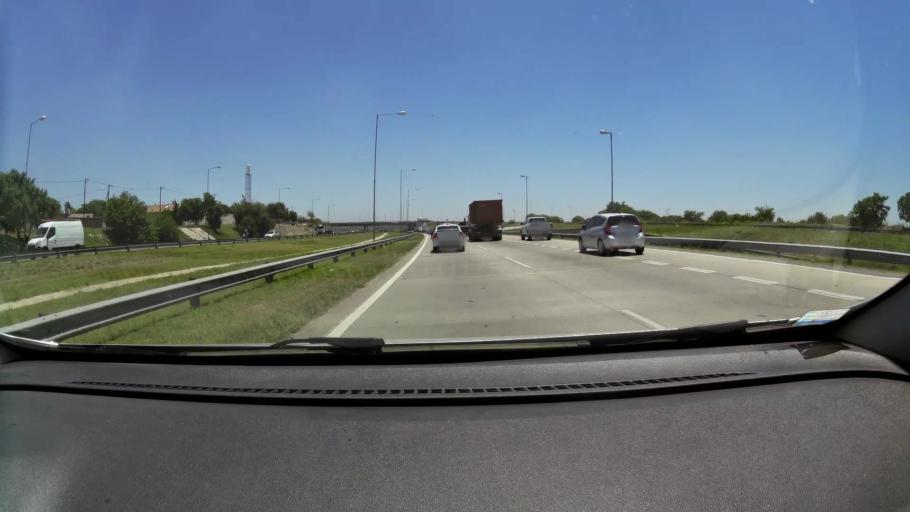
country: AR
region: Cordoba
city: Malvinas Argentinas
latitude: -31.4248
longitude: -64.1090
